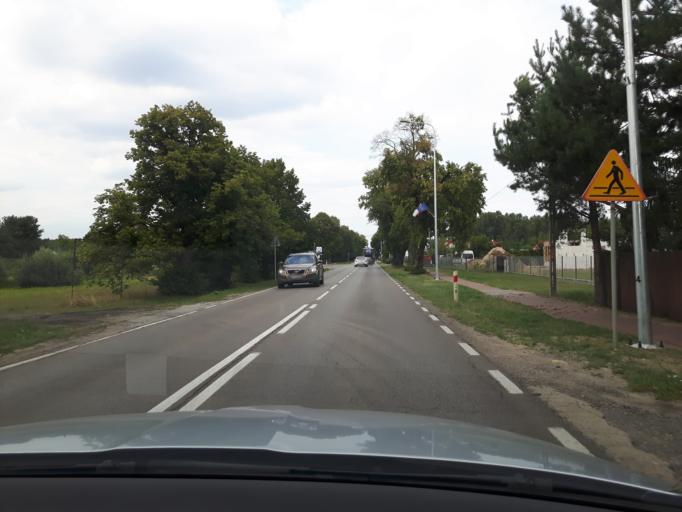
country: PL
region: Masovian Voivodeship
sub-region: Powiat legionowski
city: Nieporet
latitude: 52.4064
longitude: 21.0385
